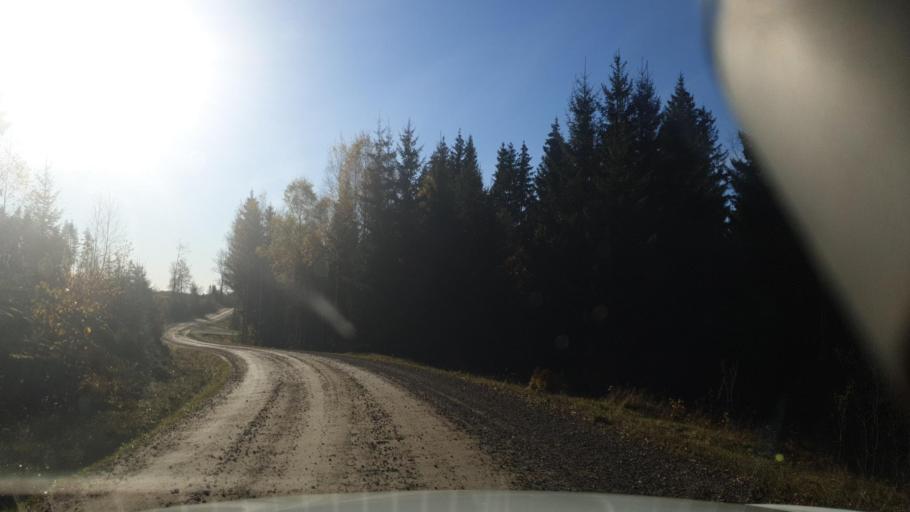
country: SE
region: Vaermland
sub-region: Karlstads Kommun
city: Edsvalla
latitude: 59.4951
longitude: 13.0288
